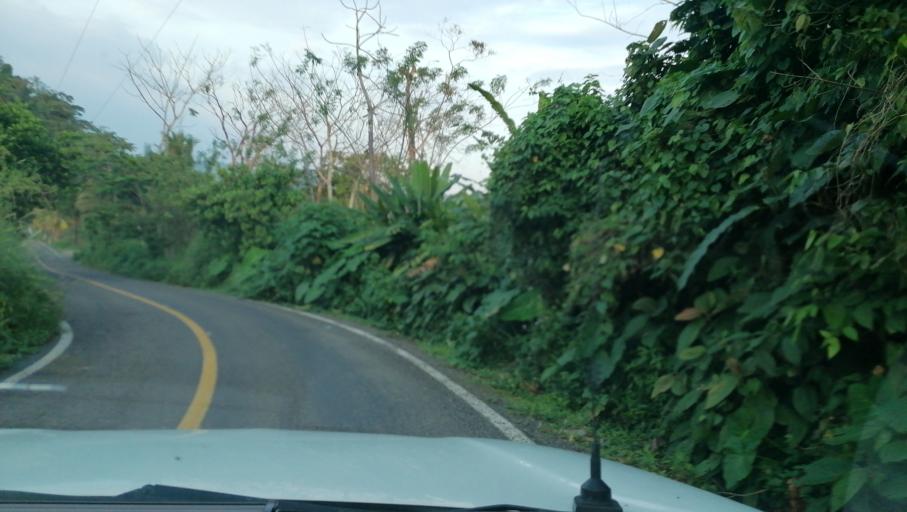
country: MX
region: Chiapas
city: Pichucalco
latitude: 17.5061
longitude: -93.2137
